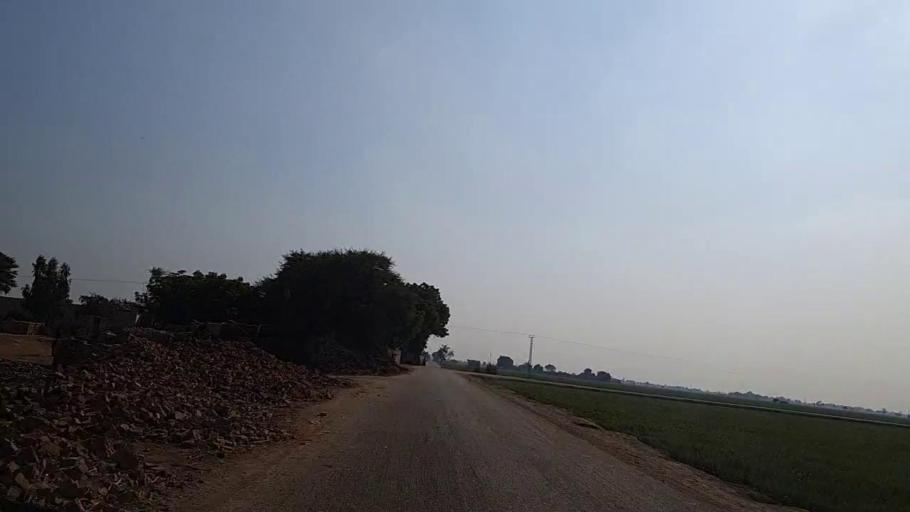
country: PK
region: Sindh
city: Sakrand
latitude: 26.0989
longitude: 68.2905
